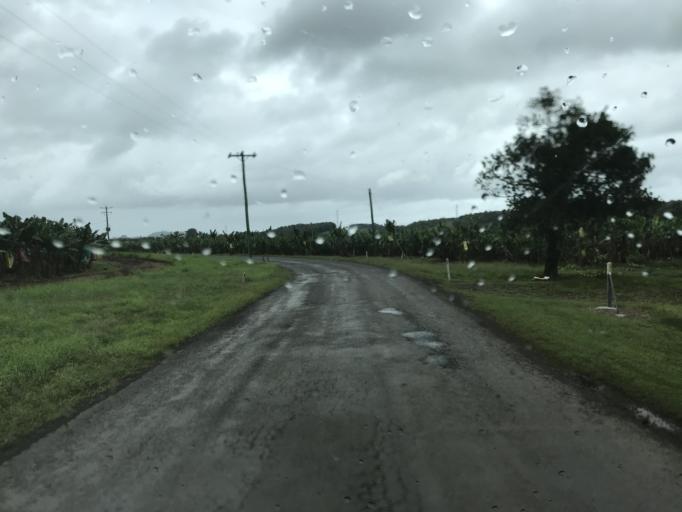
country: AU
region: Queensland
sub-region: Cassowary Coast
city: Innisfail
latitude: -17.5043
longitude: 145.9800
